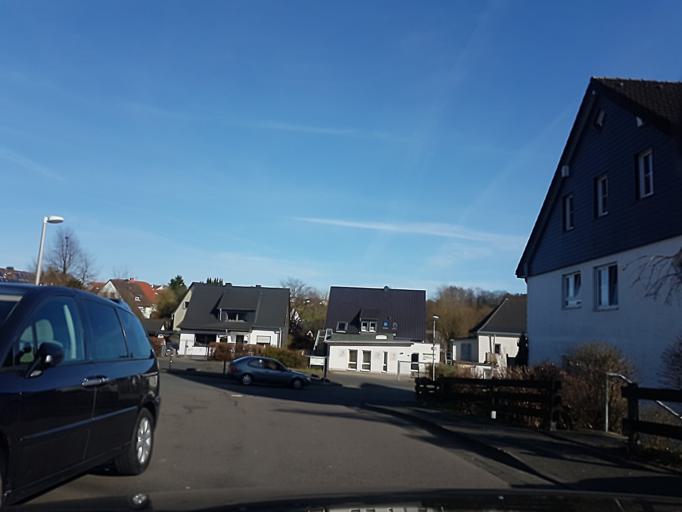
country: DE
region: North Rhine-Westphalia
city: Kierspe
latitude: 51.1389
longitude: 7.5878
